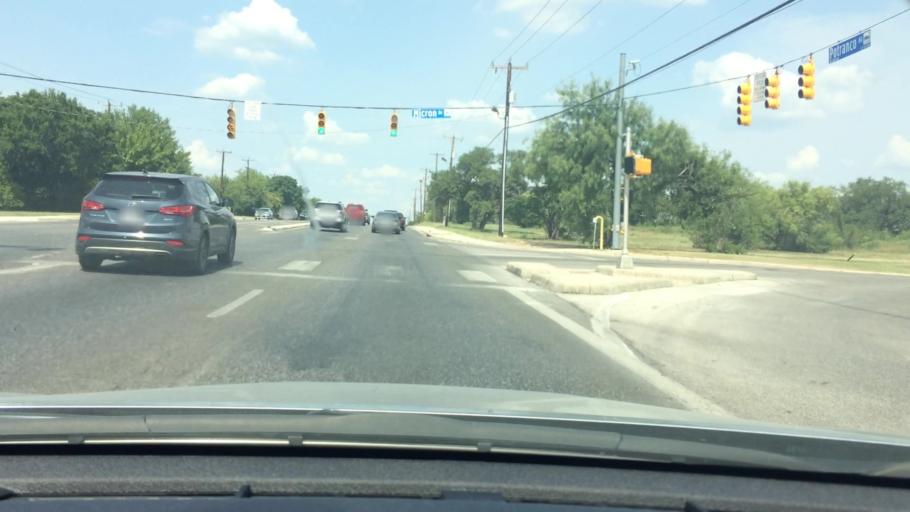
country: US
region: Texas
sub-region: Bexar County
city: Leon Valley
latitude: 29.4516
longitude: -98.6414
